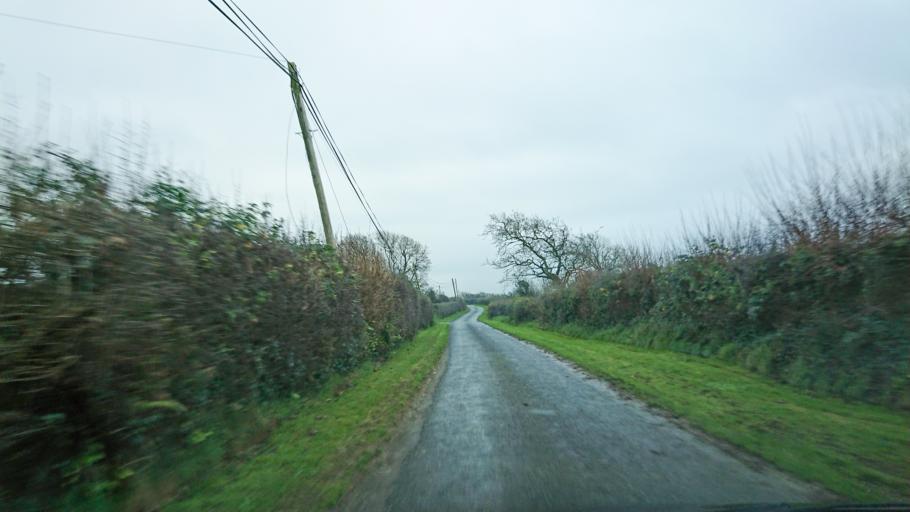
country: IE
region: Munster
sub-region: Waterford
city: Dunmore East
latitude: 52.2048
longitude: -6.9950
